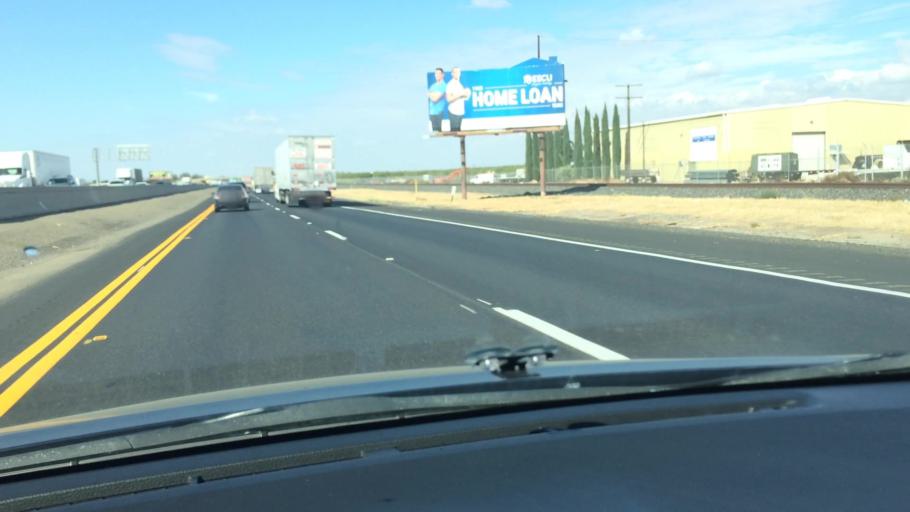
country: US
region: California
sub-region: Madera County
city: Parkwood
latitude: 36.9296
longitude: -120.0269
